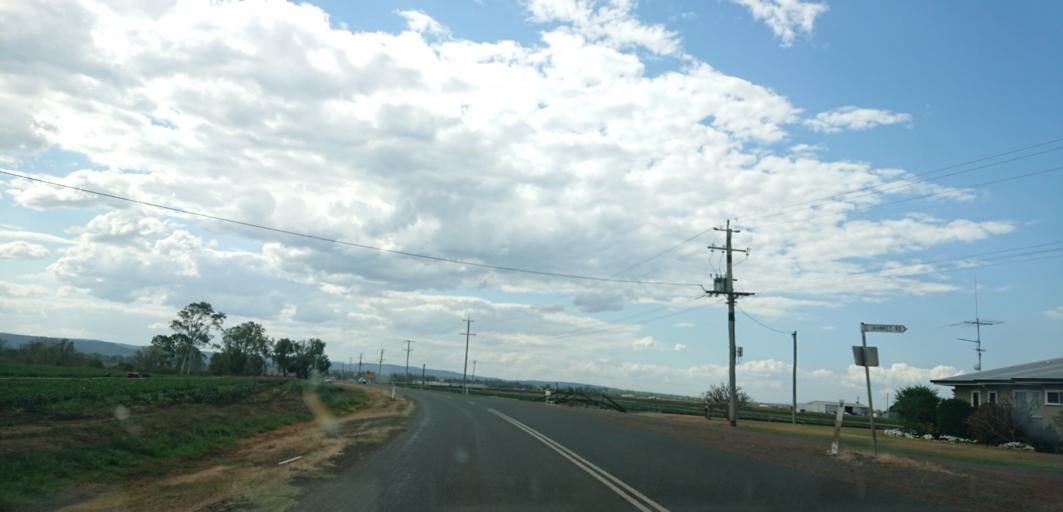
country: AU
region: Queensland
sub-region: Lockyer Valley
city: Gatton
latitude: -27.5926
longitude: 152.2267
